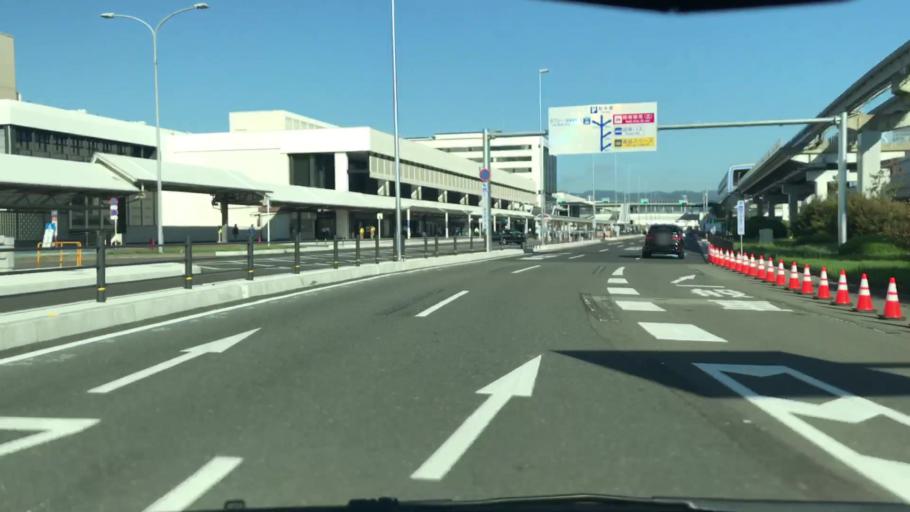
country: JP
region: Osaka
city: Toyonaka
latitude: 34.7893
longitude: 135.4443
